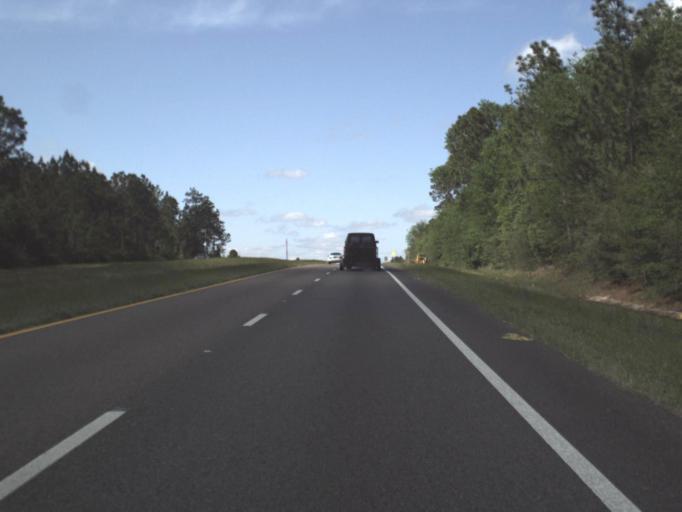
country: US
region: Florida
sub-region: Escambia County
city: Molino
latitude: 30.6927
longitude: -87.3506
